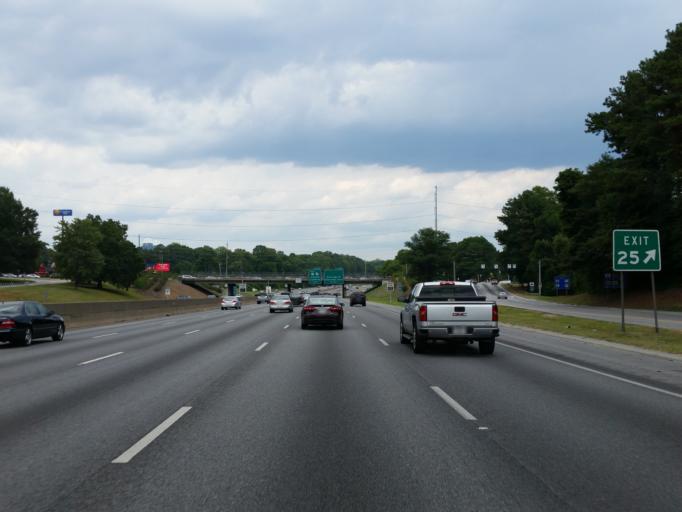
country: US
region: Georgia
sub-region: Fulton County
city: Sandy Springs
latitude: 33.9121
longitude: -84.3820
